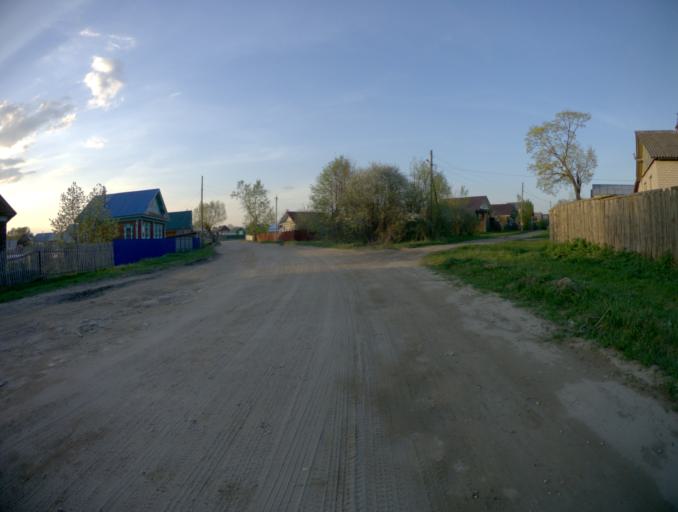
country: RU
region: Ivanovo
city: Yuzha
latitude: 56.5879
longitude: 42.0298
